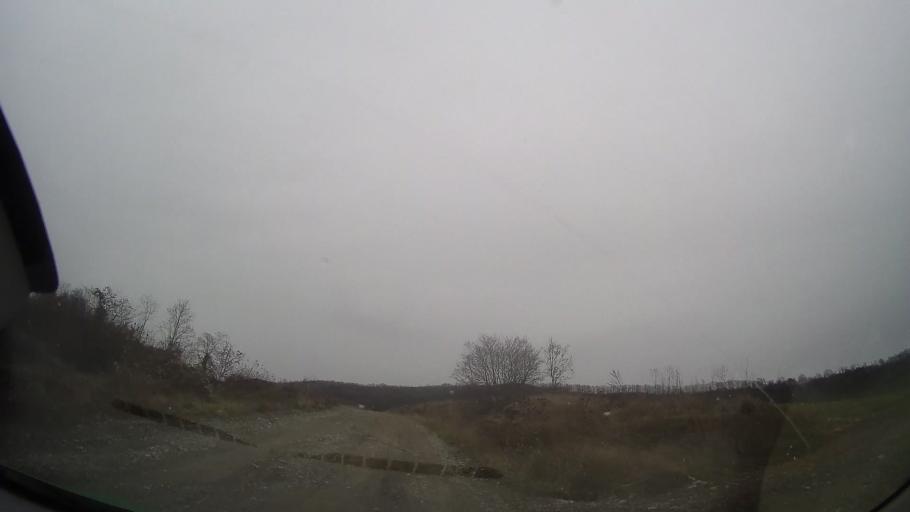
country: RO
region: Mures
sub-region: Comuna Ceausu de Campie
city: Ceausu de Campie
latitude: 46.6479
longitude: 24.4976
